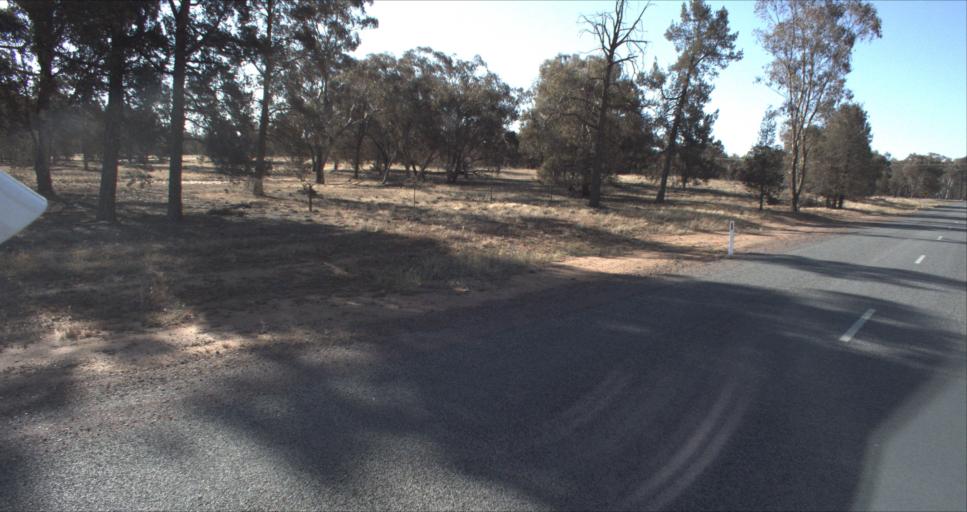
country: AU
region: New South Wales
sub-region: Leeton
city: Leeton
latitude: -34.6459
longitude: 146.3522
